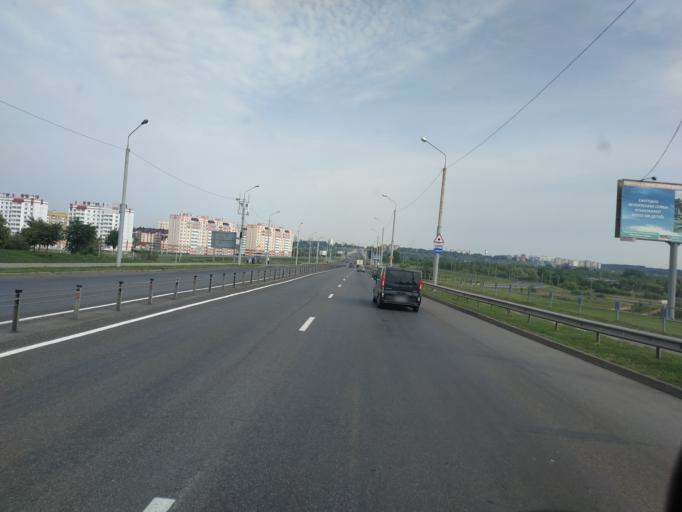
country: BY
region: Mogilev
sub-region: Mahilyowski Rayon
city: Veyno
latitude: 53.8805
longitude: 30.3826
